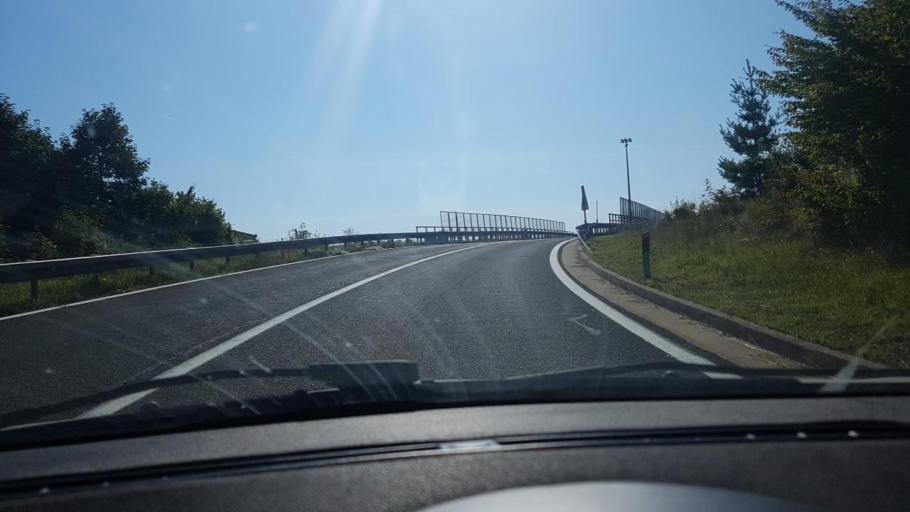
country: HR
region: Primorsko-Goranska
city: Vrbovsko
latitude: 45.3644
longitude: 15.0835
